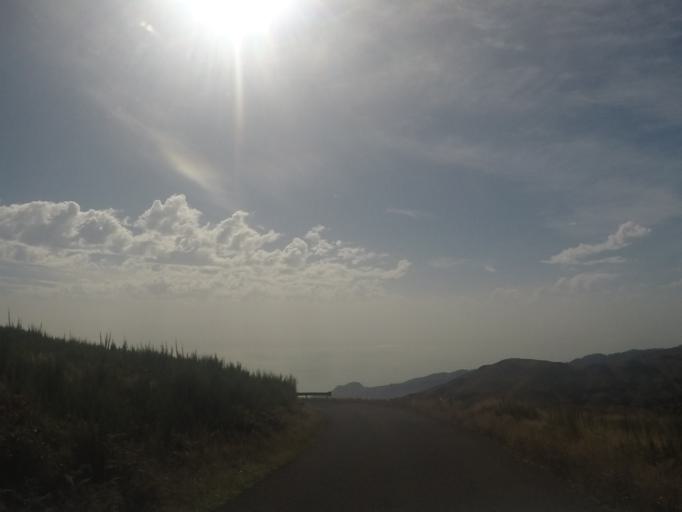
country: PT
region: Madeira
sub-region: Funchal
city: Nossa Senhora do Monte
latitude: 32.7084
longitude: -16.9143
